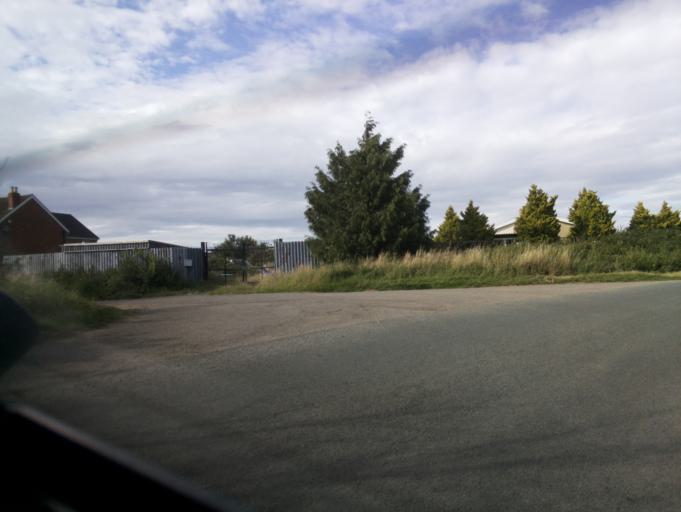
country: GB
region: England
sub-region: Gloucestershire
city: Gloucester
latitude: 51.8110
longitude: -2.2590
